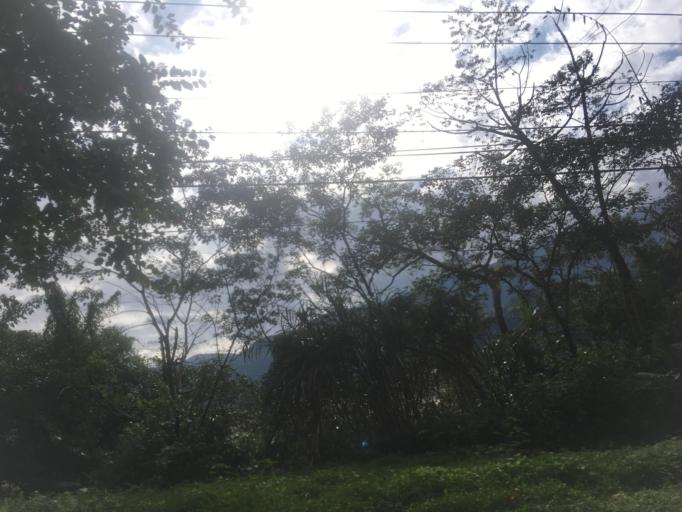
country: TW
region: Taiwan
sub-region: Yilan
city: Yilan
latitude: 24.6479
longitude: 121.5677
